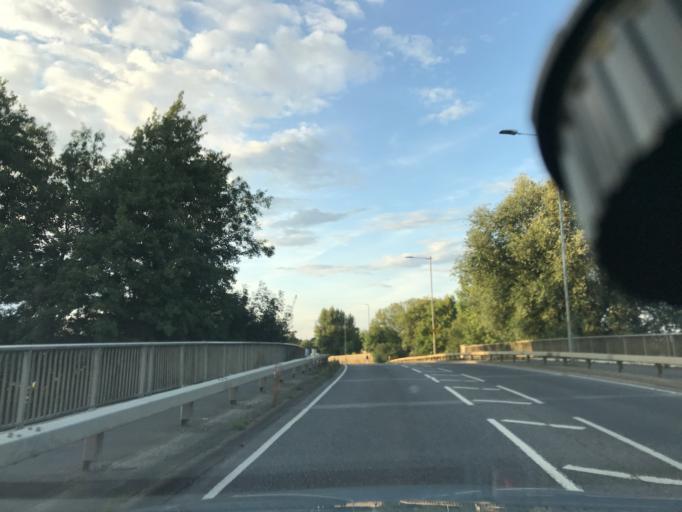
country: GB
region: England
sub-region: Buckinghamshire
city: Aylesbury
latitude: 51.8188
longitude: -0.7899
